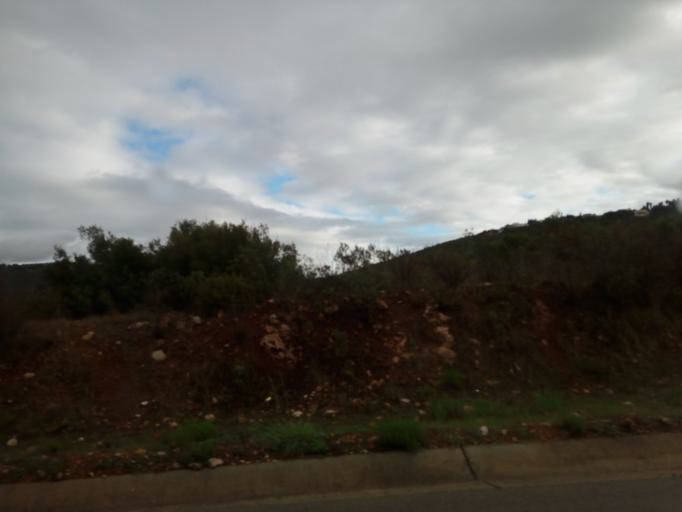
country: PT
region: Faro
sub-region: Loule
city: Loule
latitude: 37.1175
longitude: -8.0102
